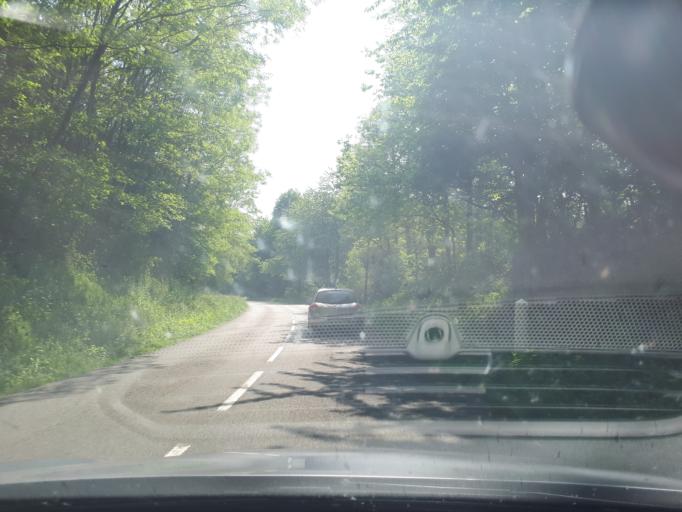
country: FR
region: Pays de la Loire
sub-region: Departement de la Sarthe
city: Le Breil-sur-Merize
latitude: 48.0208
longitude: 0.4529
